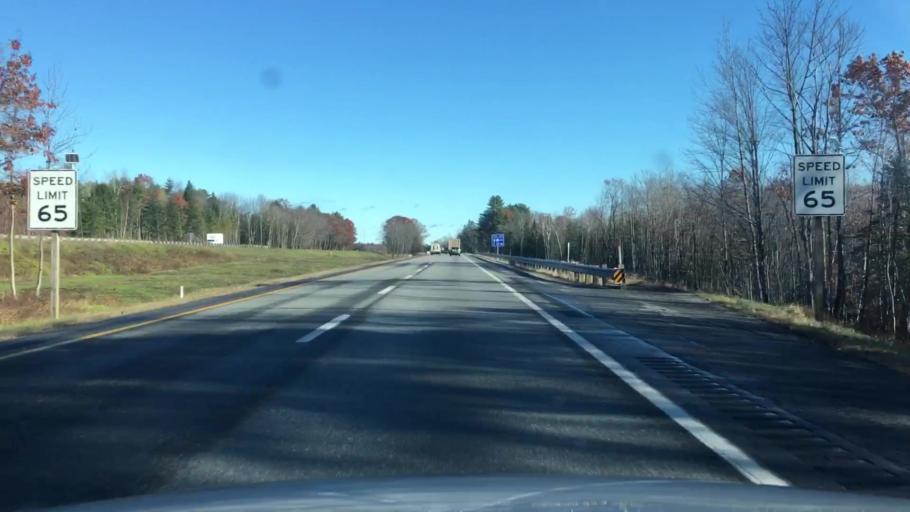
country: US
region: Maine
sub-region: Kennebec County
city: Oakland
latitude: 44.5366
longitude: -69.6857
